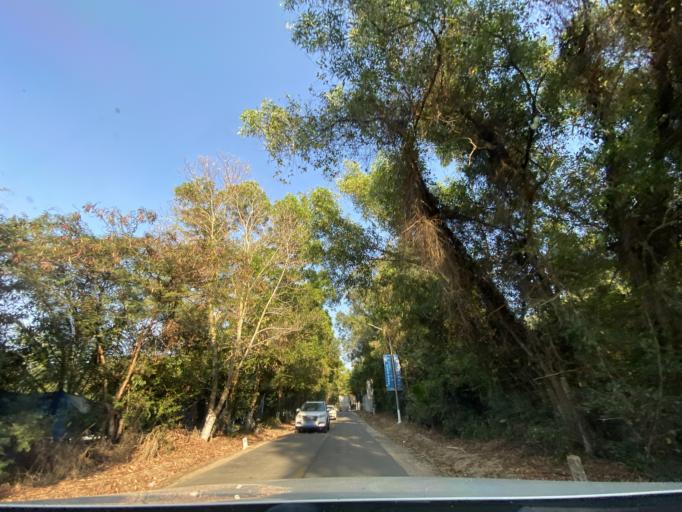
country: CN
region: Hainan
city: Yingzhou
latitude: 18.3876
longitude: 109.8234
